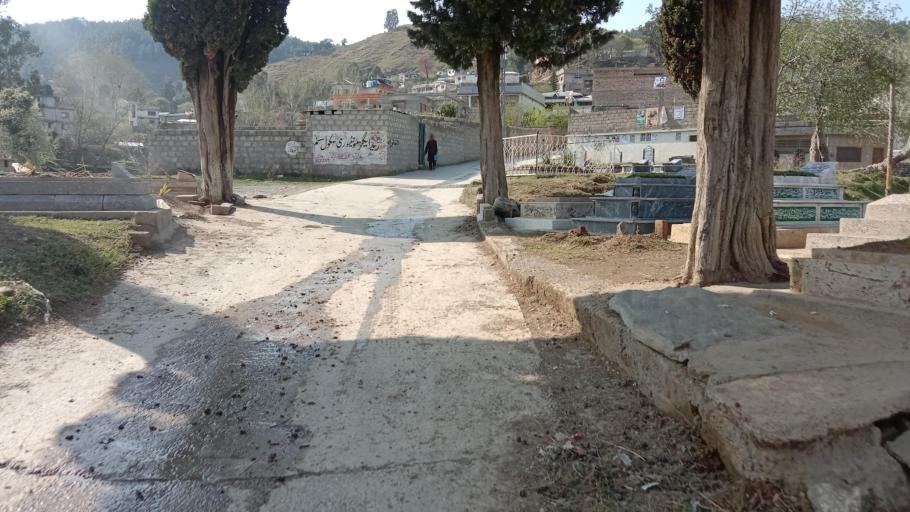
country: PK
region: Khyber Pakhtunkhwa
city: Abbottabad
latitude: 34.1760
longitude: 73.2130
